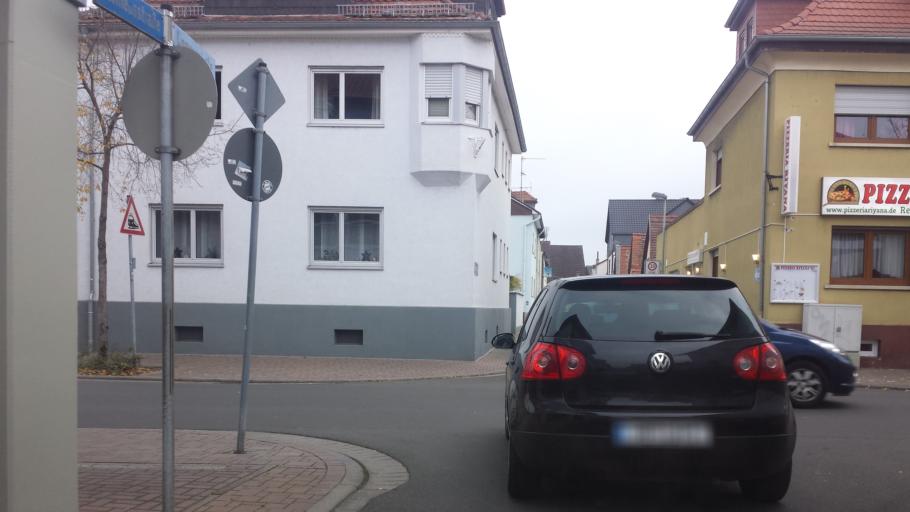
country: DE
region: Hesse
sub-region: Regierungsbezirk Darmstadt
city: Burstadt
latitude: 49.6452
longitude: 8.4541
